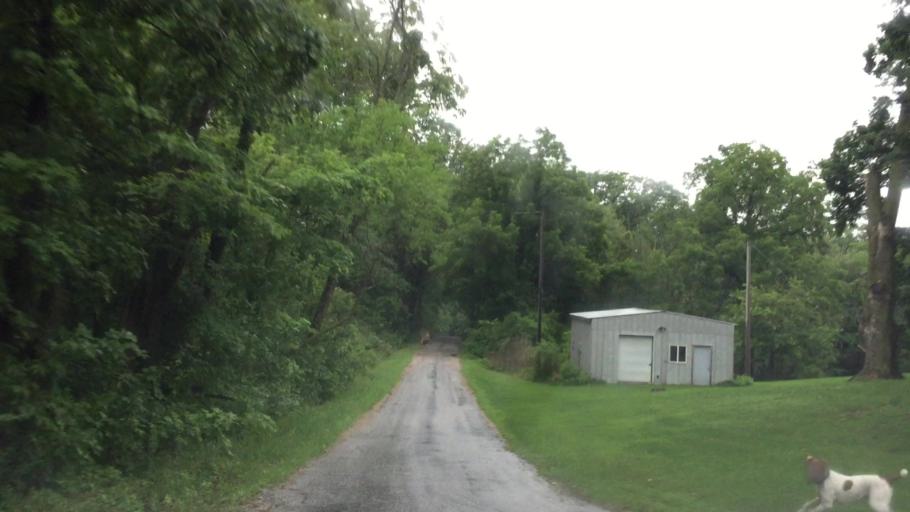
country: US
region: Iowa
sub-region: Lee County
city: Fort Madison
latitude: 40.6065
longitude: -91.2746
